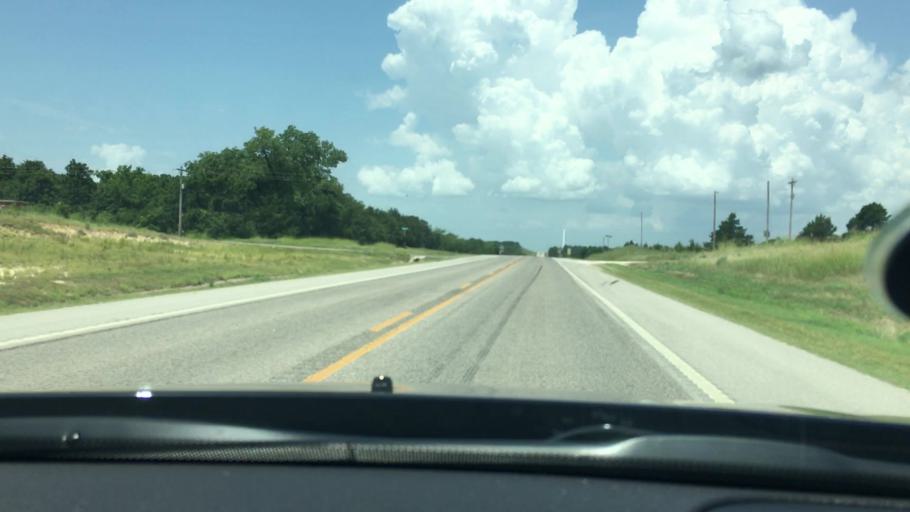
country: US
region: Oklahoma
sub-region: Carter County
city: Dickson
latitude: 34.1003
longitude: -96.9321
